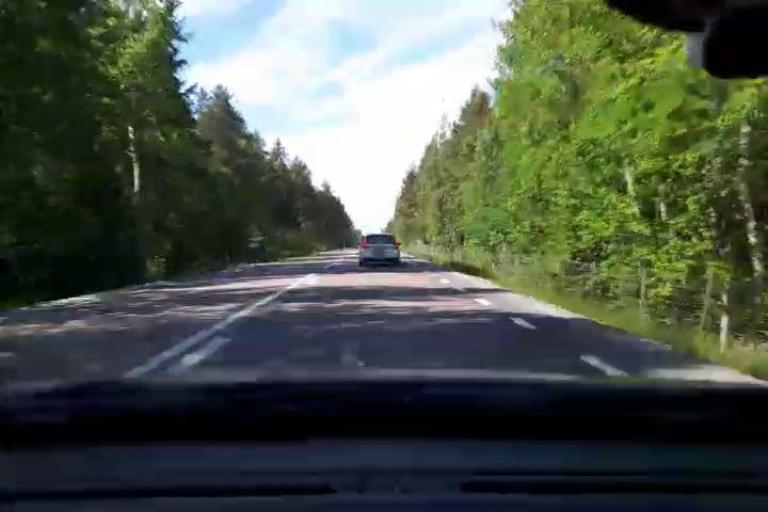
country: SE
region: Gaevleborg
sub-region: Bollnas Kommun
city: Kilafors
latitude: 61.2773
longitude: 16.5239
